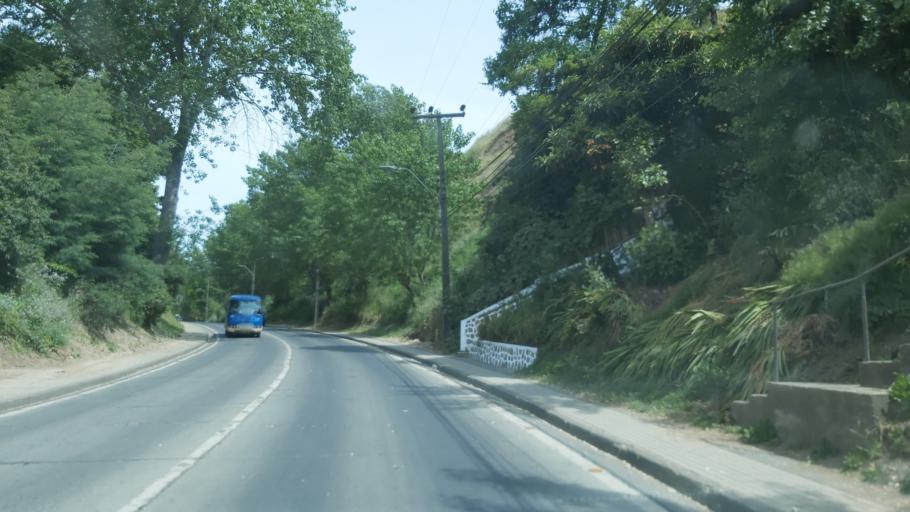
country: CL
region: Maule
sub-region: Provincia de Talca
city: Constitucion
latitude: -35.3282
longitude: -72.4200
